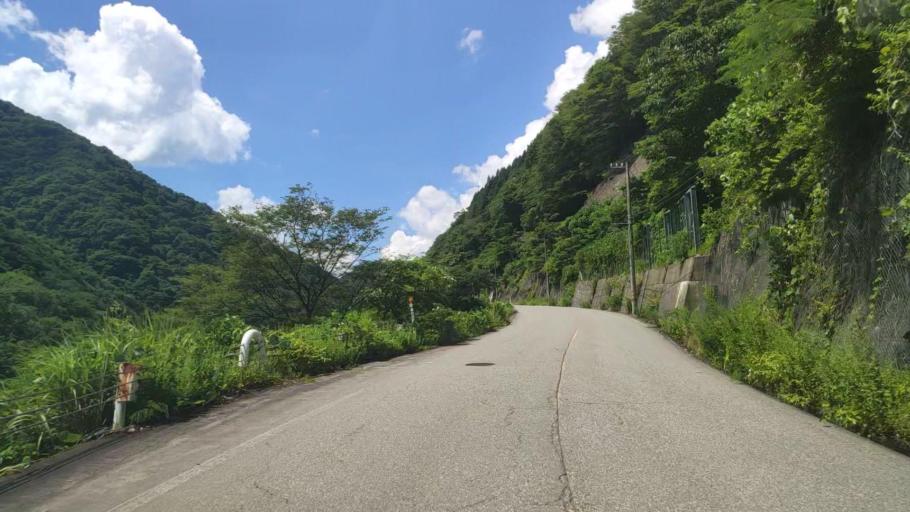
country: JP
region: Fukui
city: Ono
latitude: 35.9316
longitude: 136.5589
